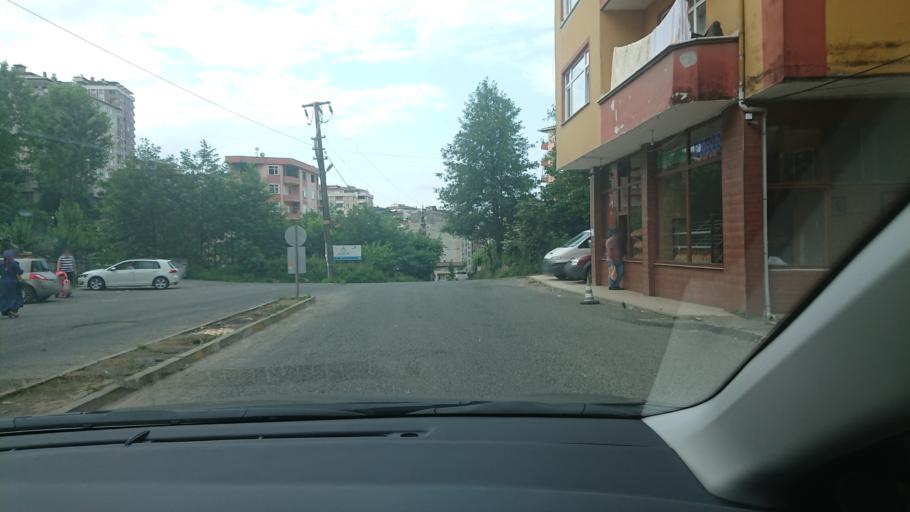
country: TR
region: Rize
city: Rize
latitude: 41.0186
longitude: 40.5161
